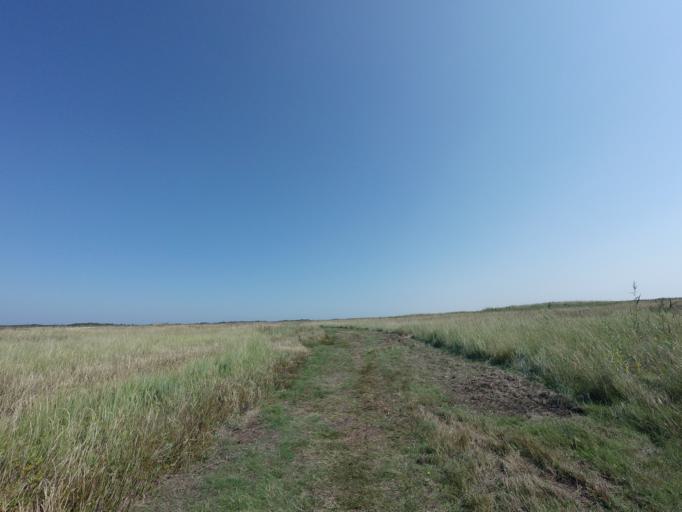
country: NL
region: Friesland
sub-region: Gemeente Schiermonnikoog
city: Schiermonnikoog
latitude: 53.4916
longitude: 6.2417
